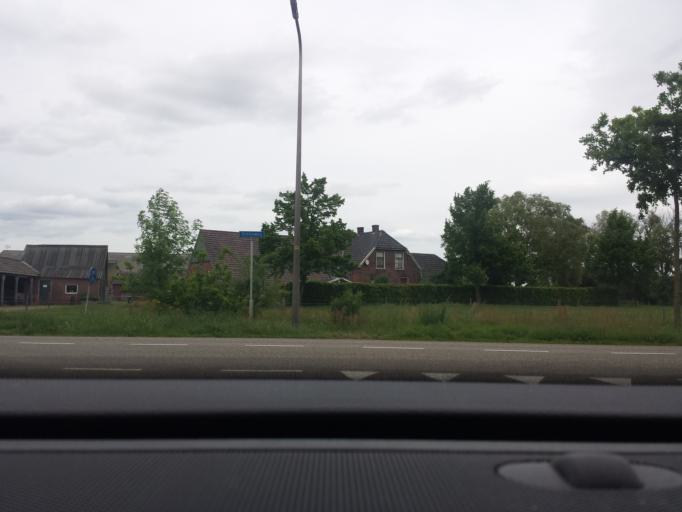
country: NL
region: Gelderland
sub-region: Oost Gelre
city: Lichtenvoorde
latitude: 52.0547
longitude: 6.5818
